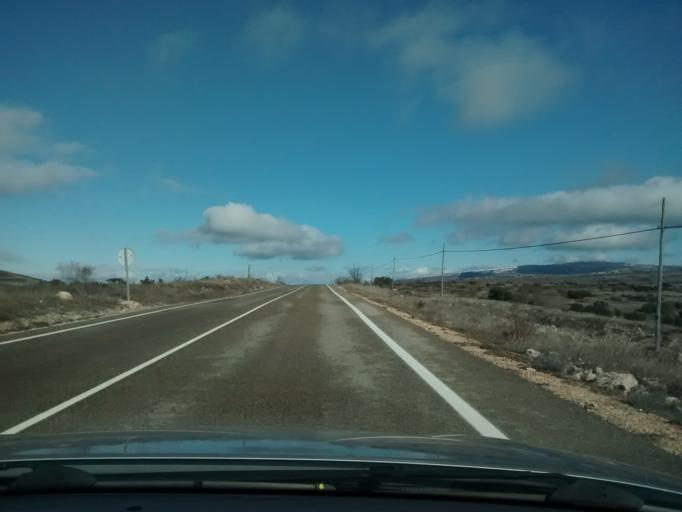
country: ES
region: Castille and Leon
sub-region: Provincia de Burgos
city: Rucandio
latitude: 42.7900
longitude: -3.6210
